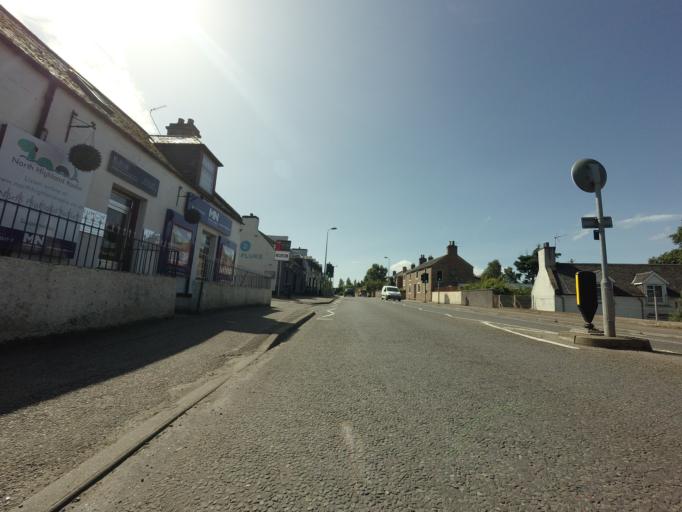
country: GB
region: Scotland
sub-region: Highland
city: Inverness
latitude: 57.4731
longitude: -4.1992
